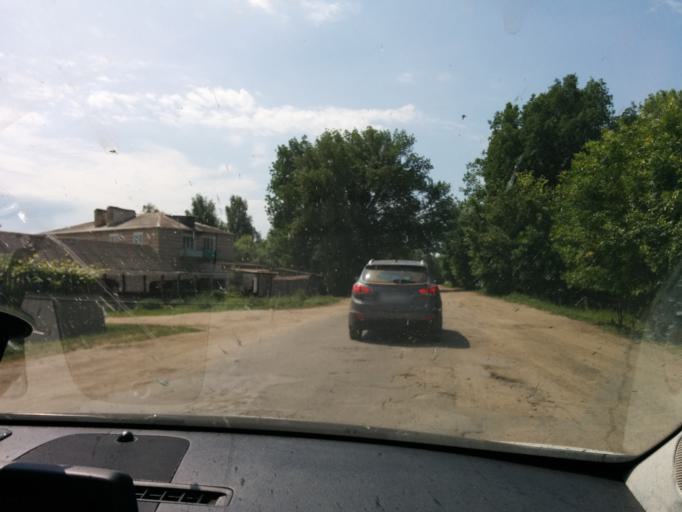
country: RU
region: Tambov
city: Morshansk
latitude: 53.6147
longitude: 41.8301
